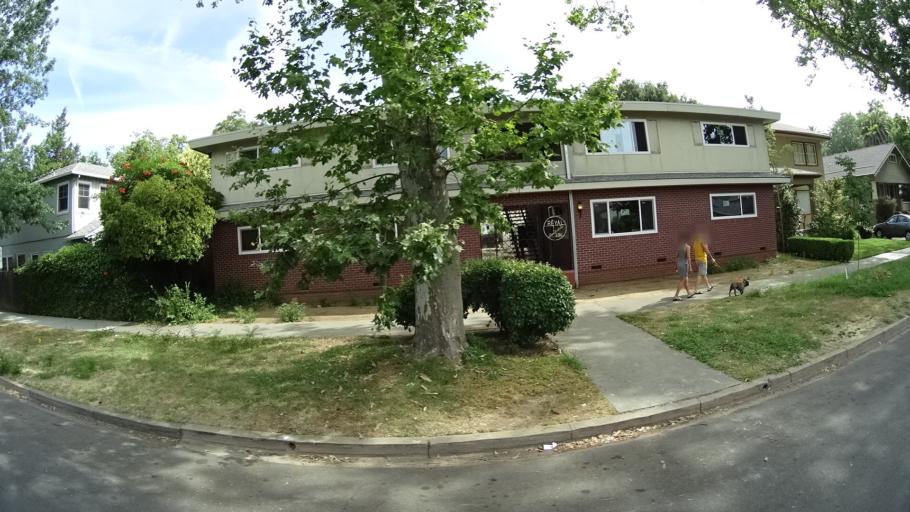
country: US
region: California
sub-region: Sacramento County
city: Sacramento
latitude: 38.5634
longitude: -121.4808
